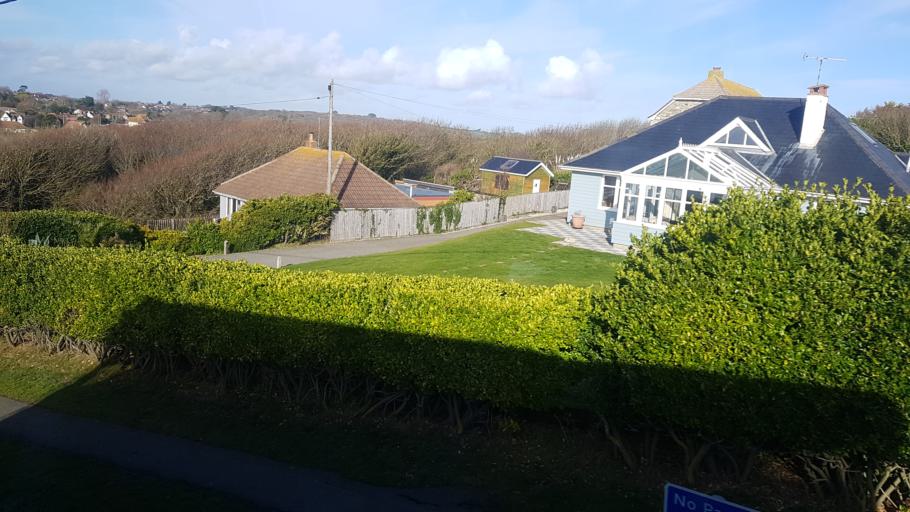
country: GB
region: England
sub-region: Isle of Wight
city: Freshwater
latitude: 50.6704
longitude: -1.5081
